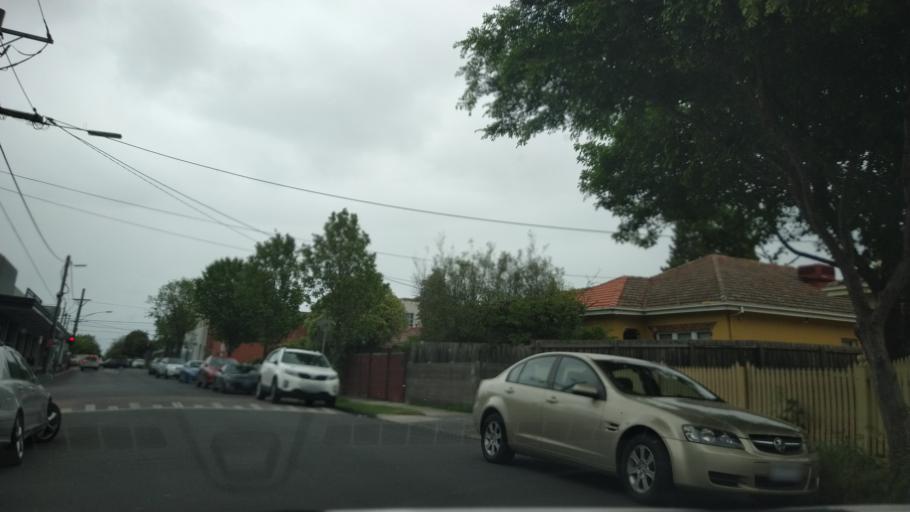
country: AU
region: Victoria
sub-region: Glen Eira
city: Glen Huntly
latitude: -37.8882
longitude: 145.0409
